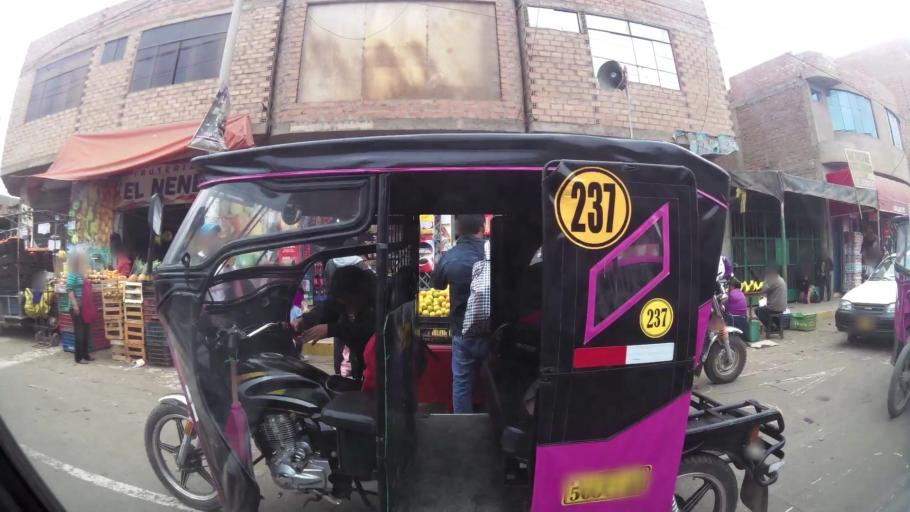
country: PE
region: Lima
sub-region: Provincia de Huaral
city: Huaral
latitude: -11.5021
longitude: -77.2033
